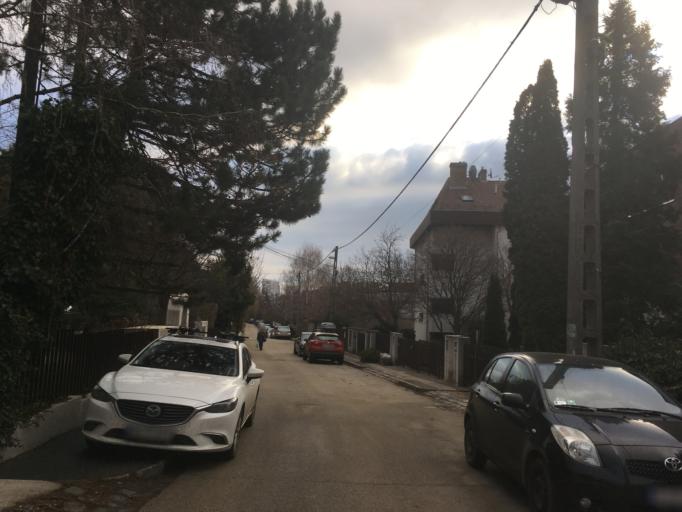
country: HU
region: Budapest
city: Budapest II. keruelet
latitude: 47.5314
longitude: 18.9896
